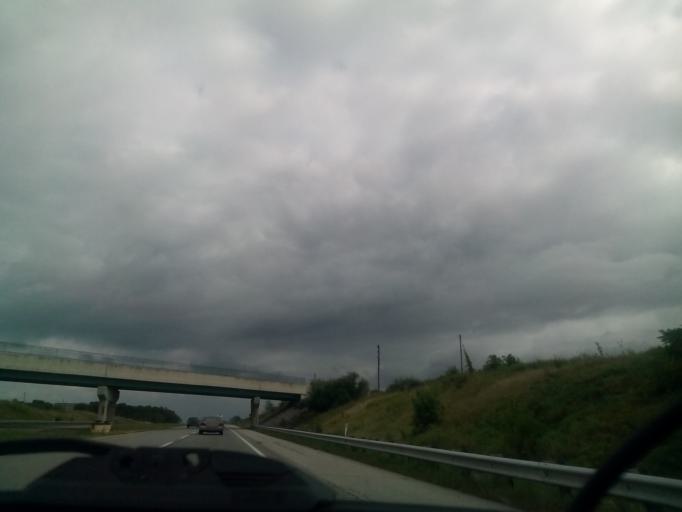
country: US
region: Indiana
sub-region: Steuben County
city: Fremont
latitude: 41.6814
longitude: -84.8790
